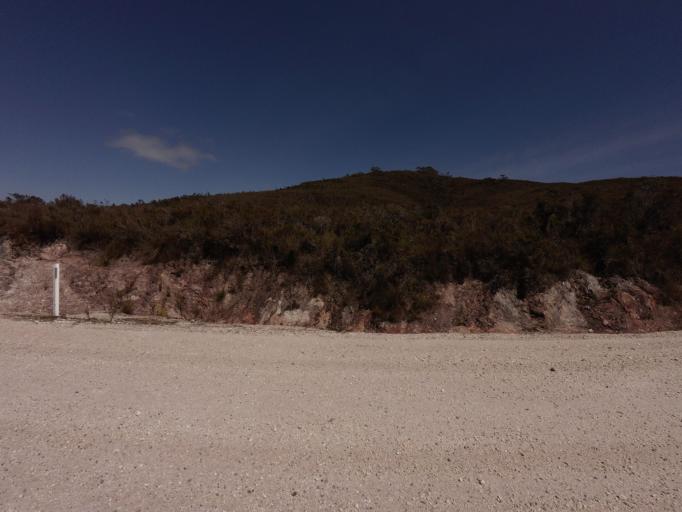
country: AU
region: Tasmania
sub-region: Huon Valley
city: Geeveston
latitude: -43.0332
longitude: 146.2928
